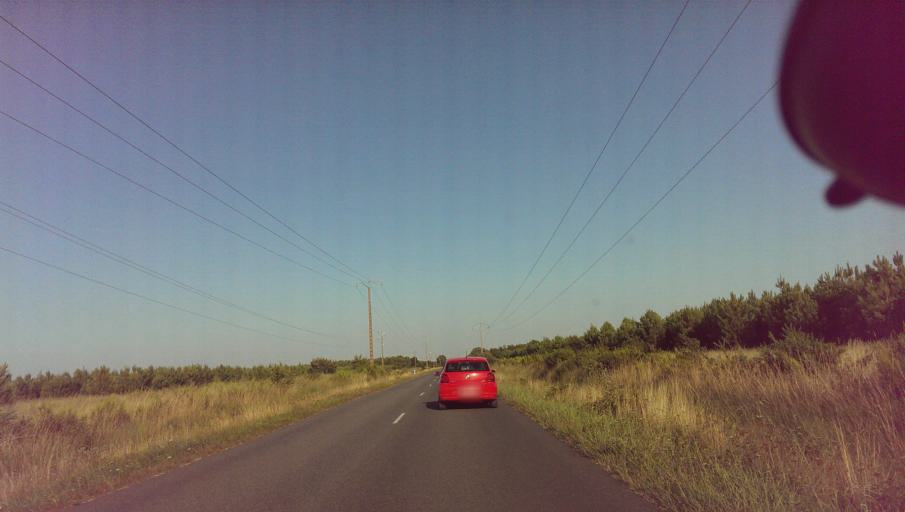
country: FR
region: Aquitaine
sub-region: Departement des Landes
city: Mimizan
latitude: 44.1842
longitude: -1.1903
